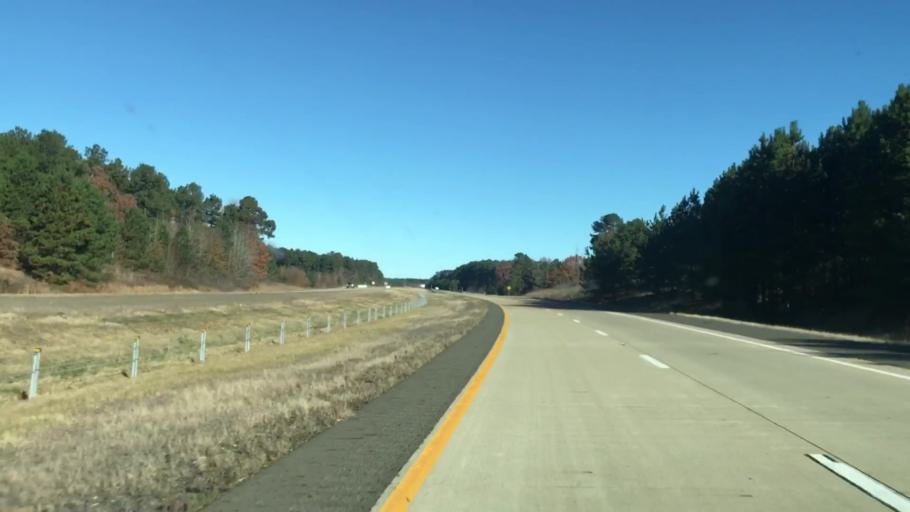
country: US
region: Louisiana
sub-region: Caddo Parish
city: Vivian
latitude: 33.0885
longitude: -93.8946
